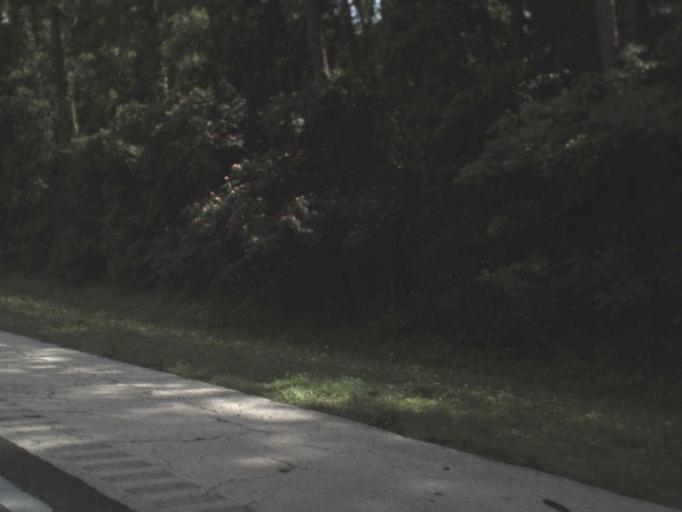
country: US
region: Florida
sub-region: Alachua County
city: High Springs
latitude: 29.8918
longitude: -82.5453
